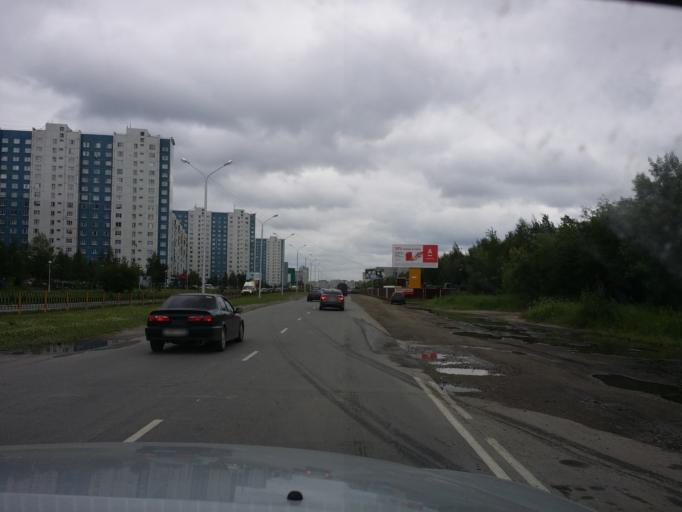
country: RU
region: Khanty-Mansiyskiy Avtonomnyy Okrug
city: Nizhnevartovsk
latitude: 60.9540
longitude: 76.5775
